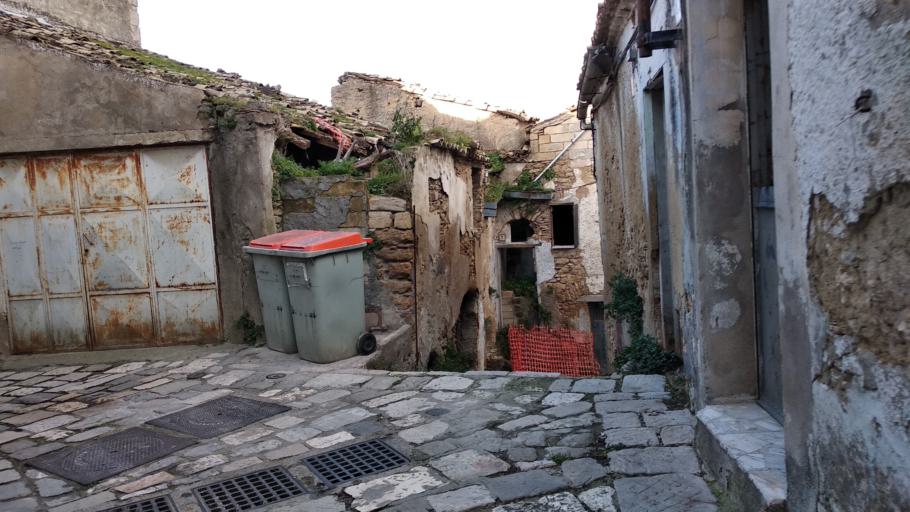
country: IT
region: Basilicate
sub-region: Provincia di Matera
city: Tricarico
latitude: 40.6256
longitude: 16.1428
